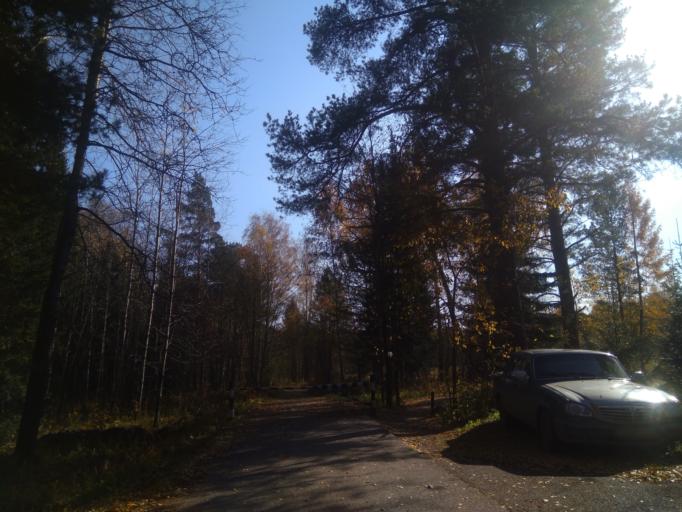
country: RU
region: Sverdlovsk
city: Mikhaylovsk
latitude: 56.5227
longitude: 59.2347
